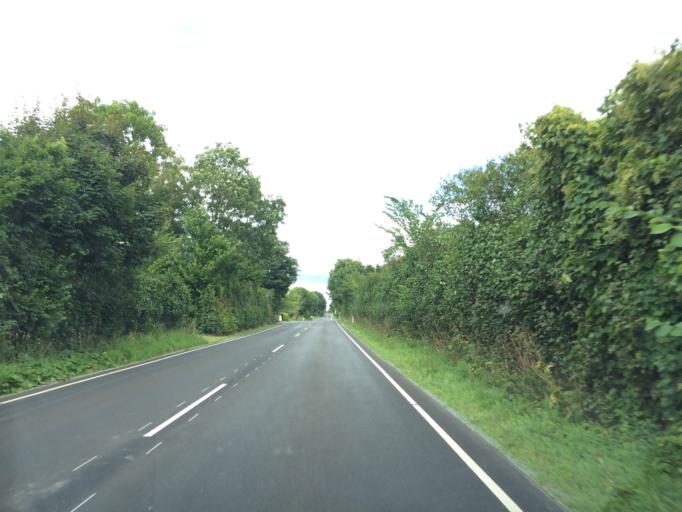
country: DK
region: South Denmark
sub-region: Odense Kommune
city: Bellinge
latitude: 55.2838
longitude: 10.2701
